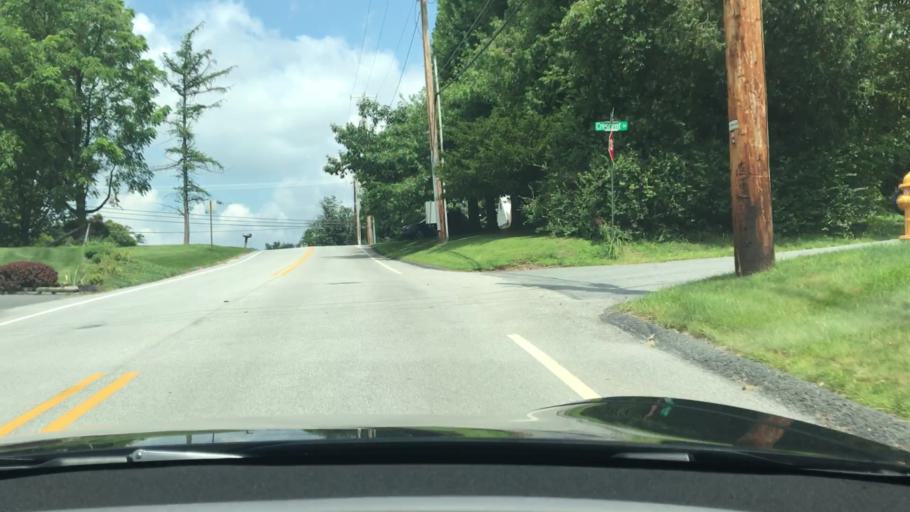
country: US
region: Pennsylvania
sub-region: Cumberland County
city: New Cumberland
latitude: 40.2029
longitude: -76.8793
